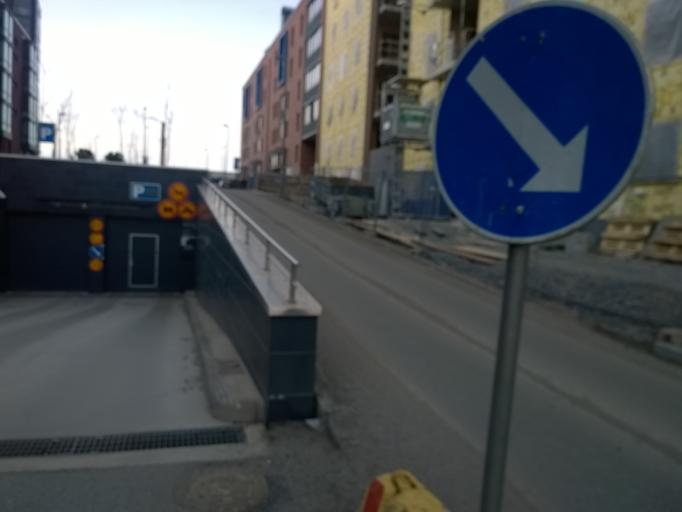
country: FI
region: Pirkanmaa
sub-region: Tampere
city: Tampere
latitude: 61.4908
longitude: 23.7650
